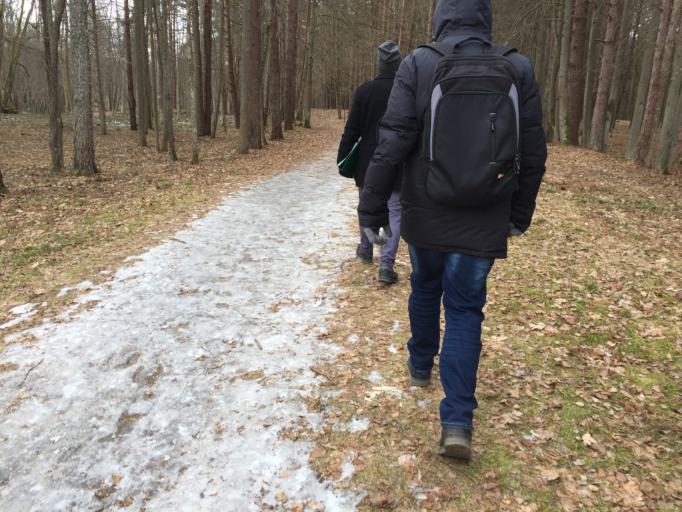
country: LV
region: Valmieras Rajons
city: Valmiera
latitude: 57.5369
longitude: 25.4441
